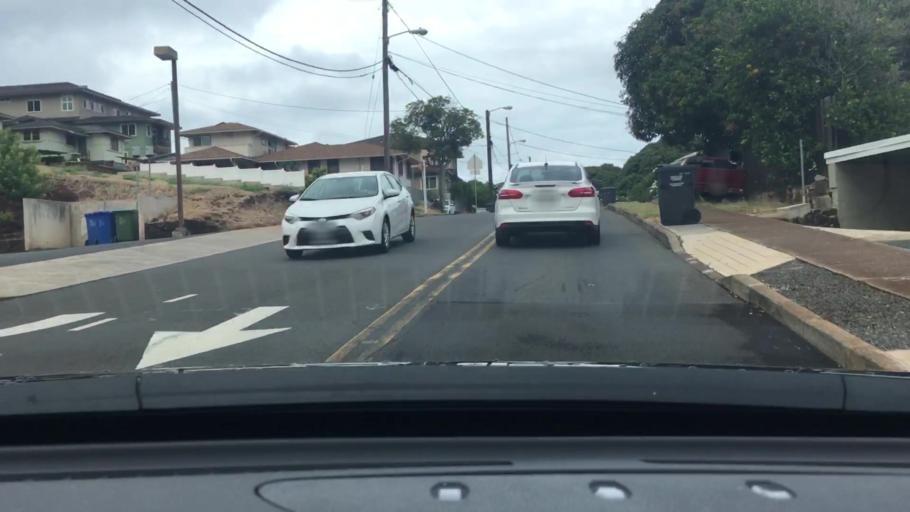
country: US
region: Hawaii
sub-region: Honolulu County
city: Honolulu
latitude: 21.2787
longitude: -157.7995
